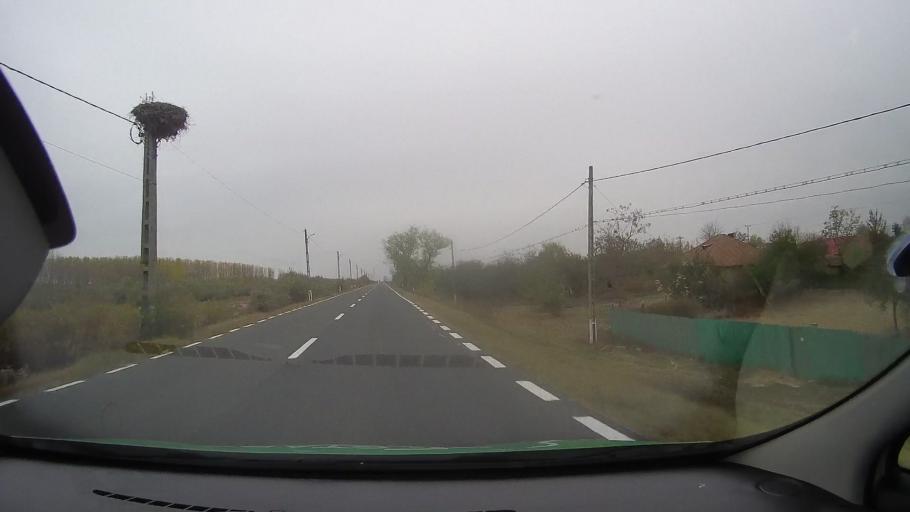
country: RO
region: Ialomita
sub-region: Comuna Giurgeni
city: Giurgeni
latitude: 44.7371
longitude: 27.8554
